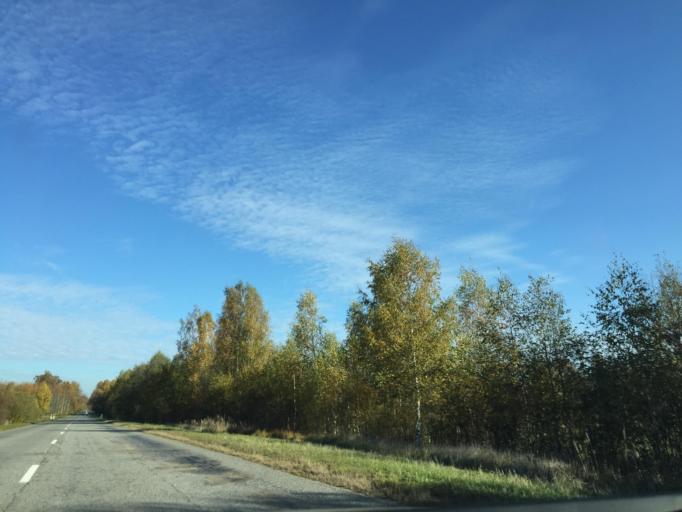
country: LV
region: Skriveri
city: Skriveri
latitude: 56.8252
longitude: 25.1235
